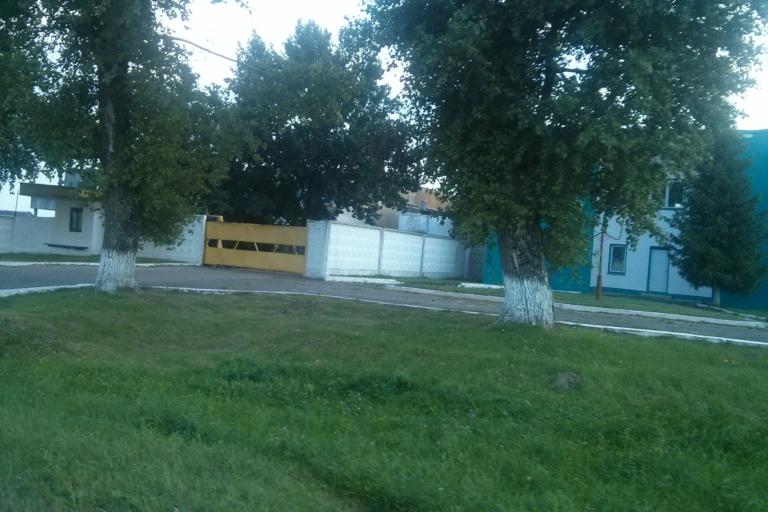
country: BY
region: Minsk
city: Chervyen'
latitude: 53.7212
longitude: 28.3895
